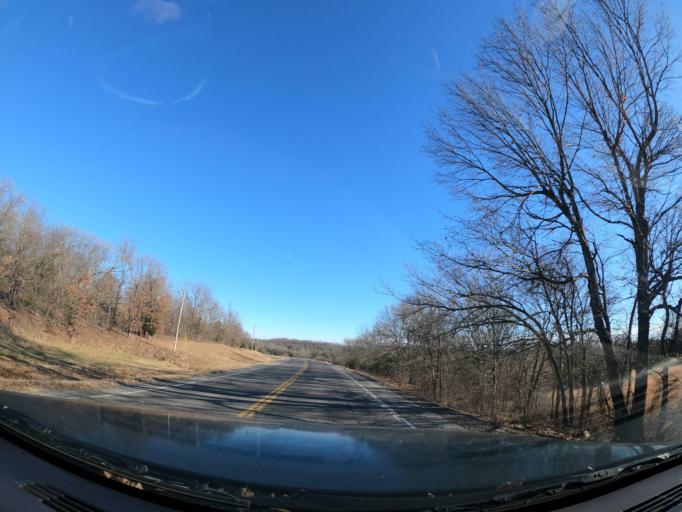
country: US
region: Oklahoma
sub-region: Pittsburg County
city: Longtown
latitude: 35.2150
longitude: -95.4213
